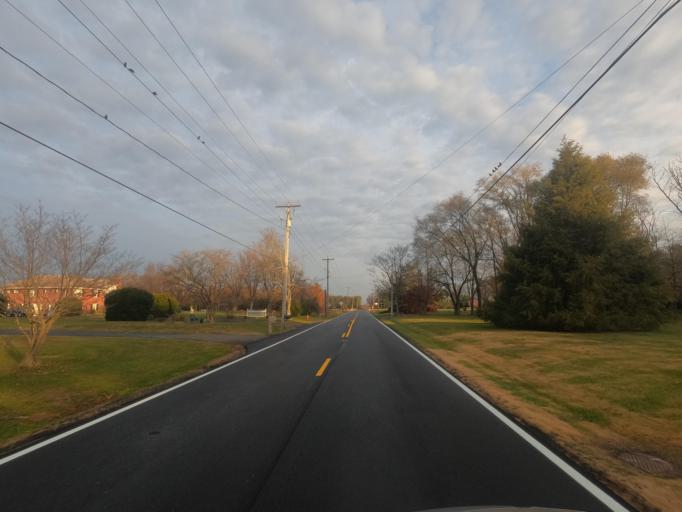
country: US
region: Delaware
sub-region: New Castle County
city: Townsend
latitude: 39.2660
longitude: -75.8379
